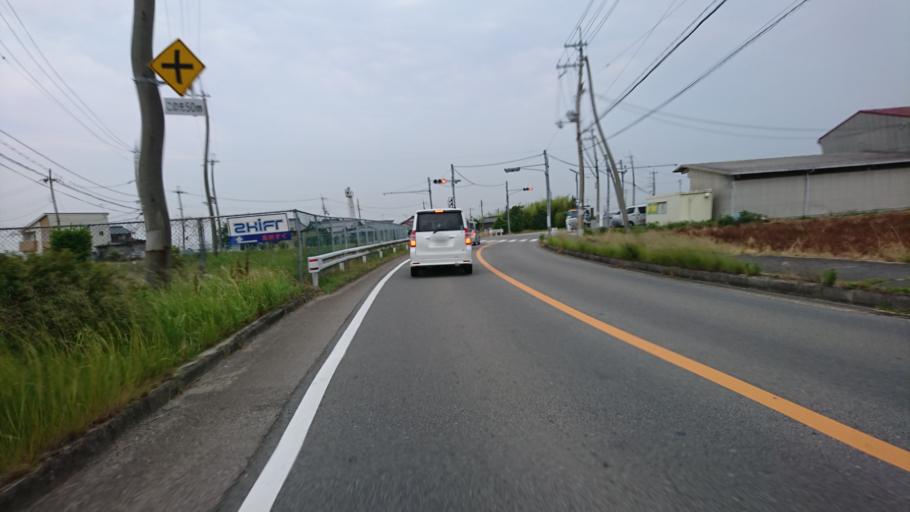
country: JP
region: Hyogo
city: Miki
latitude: 34.7376
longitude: 134.9662
